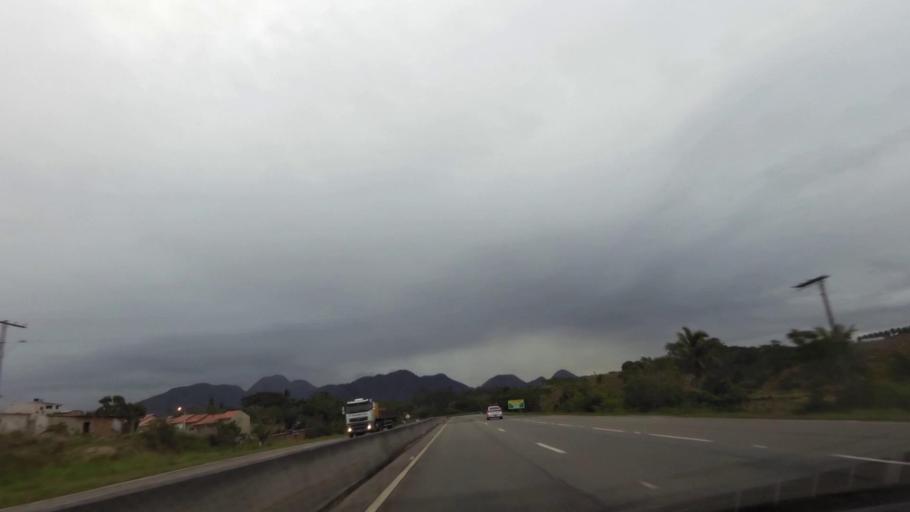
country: BR
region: Espirito Santo
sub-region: Guarapari
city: Guarapari
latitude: -20.6131
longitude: -40.4556
